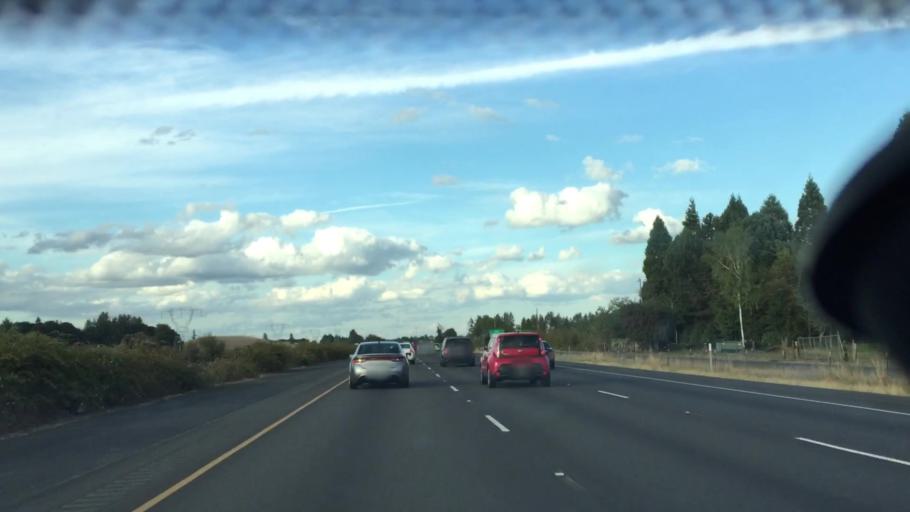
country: US
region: Oregon
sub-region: Marion County
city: Woodburn
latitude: 45.1684
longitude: -122.8626
